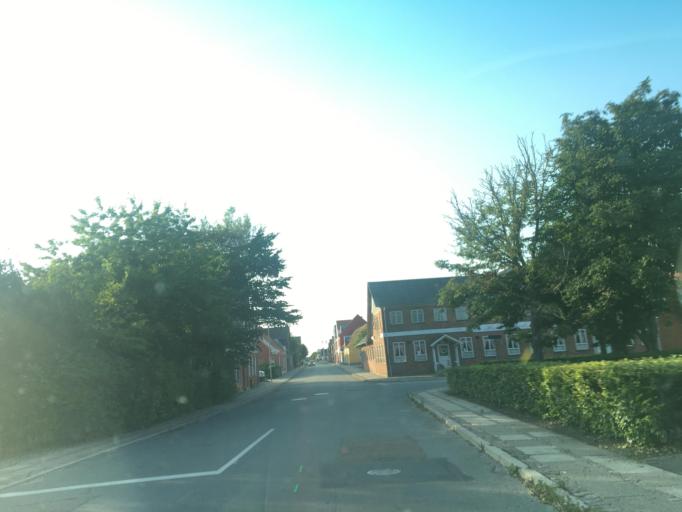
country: DK
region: North Denmark
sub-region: Thisted Kommune
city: Hurup
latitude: 56.8061
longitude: 8.4067
